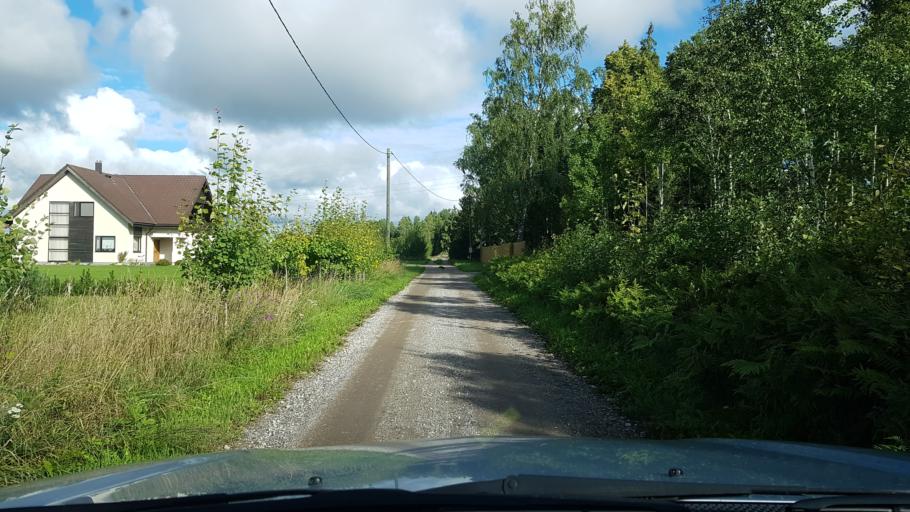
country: EE
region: Harju
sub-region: Rae vald
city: Vaida
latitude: 59.2670
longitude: 25.0235
